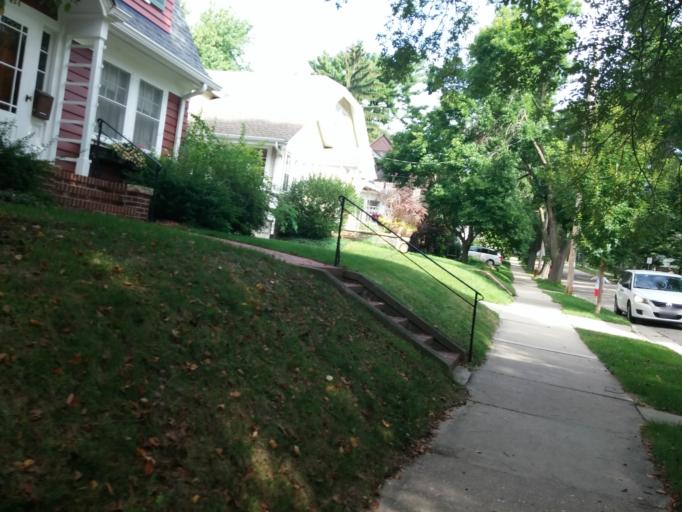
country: US
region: Wisconsin
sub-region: Dane County
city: Shorewood Hills
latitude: 43.0633
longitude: -89.4272
